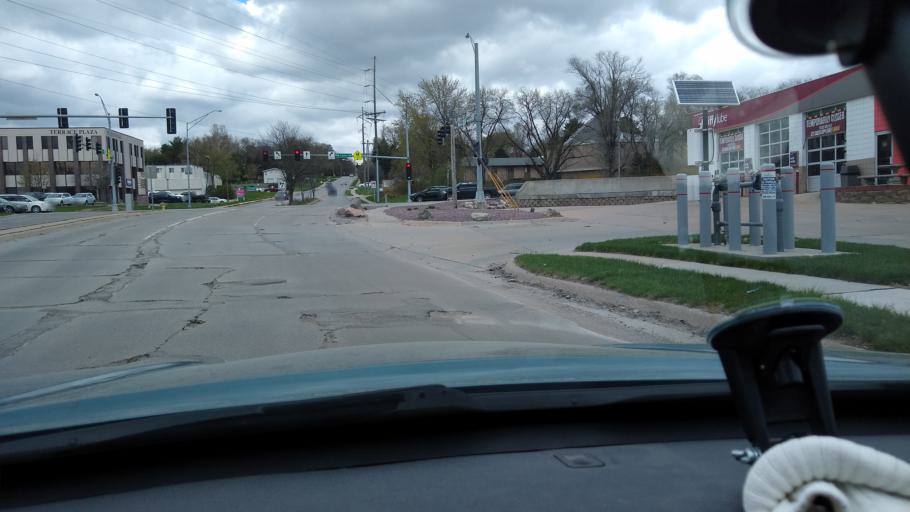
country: US
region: Nebraska
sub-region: Douglas County
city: Ralston
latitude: 41.2335
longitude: -96.0910
